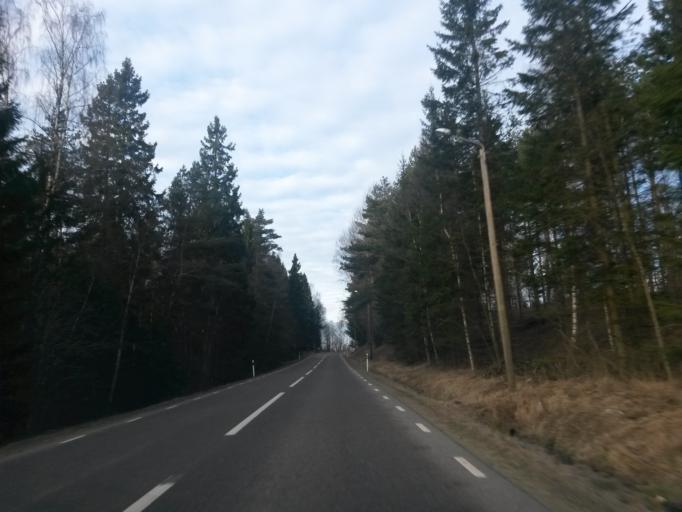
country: SE
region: Vaestra Goetaland
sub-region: Vargarda Kommun
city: Vargarda
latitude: 57.9021
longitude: 12.9111
